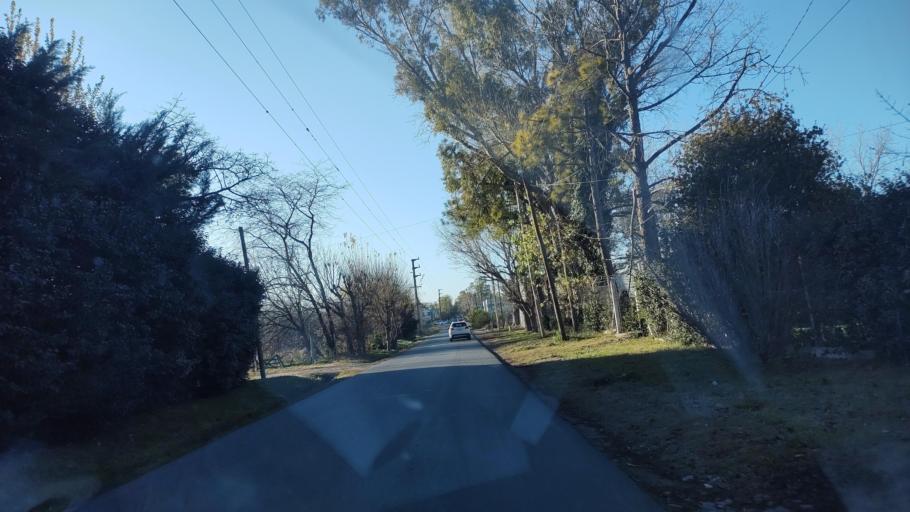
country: AR
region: Buenos Aires
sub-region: Partido de La Plata
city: La Plata
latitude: -34.8841
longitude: -58.0732
